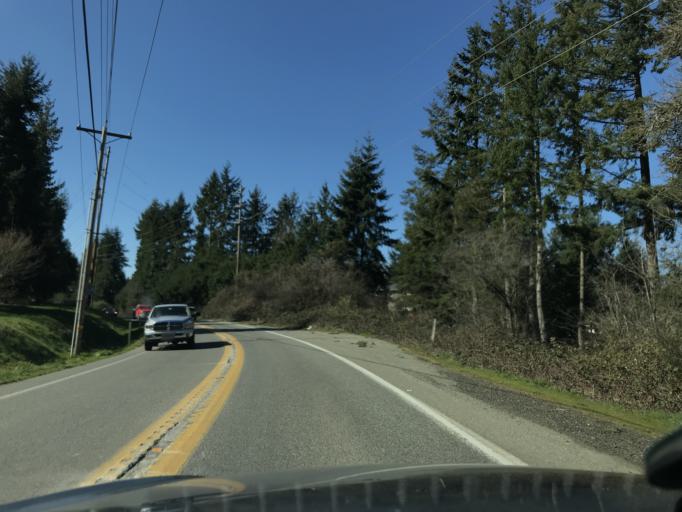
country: US
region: Washington
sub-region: Pierce County
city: Wauna
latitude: 47.3886
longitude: -122.6583
